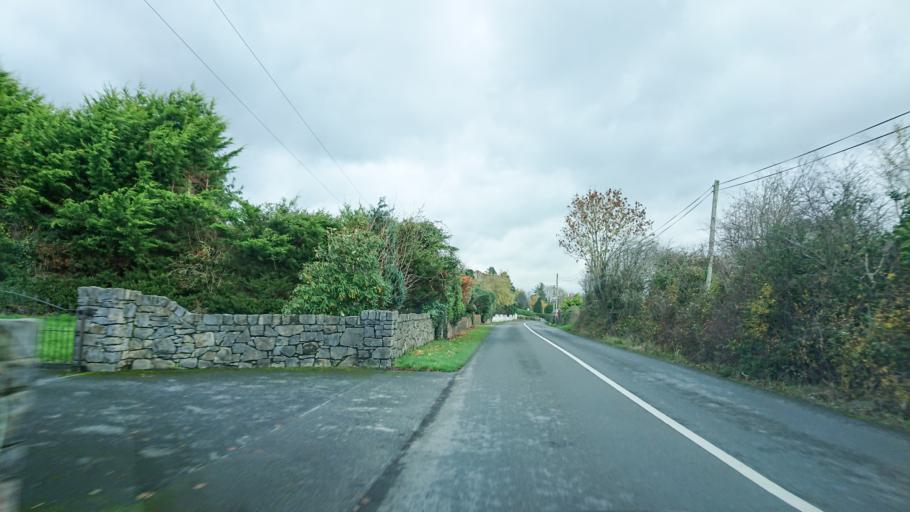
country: IE
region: Munster
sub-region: South Tipperary
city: Cluain Meala
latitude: 52.3560
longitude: -7.6564
